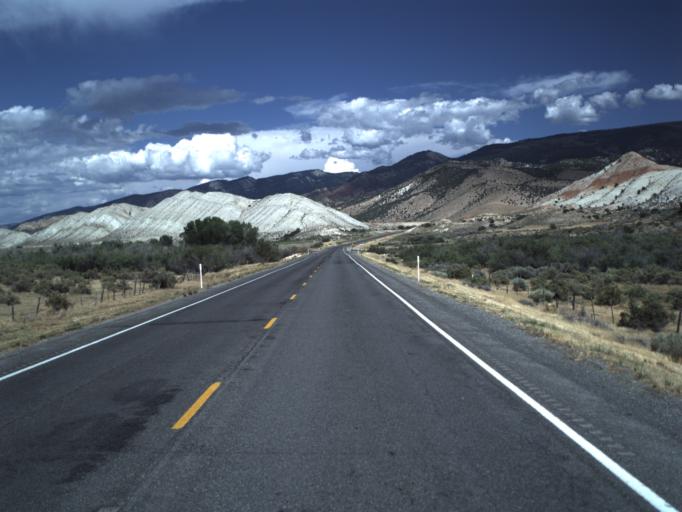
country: US
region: Utah
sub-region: Sanpete County
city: Gunnison
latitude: 39.1651
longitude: -111.7324
